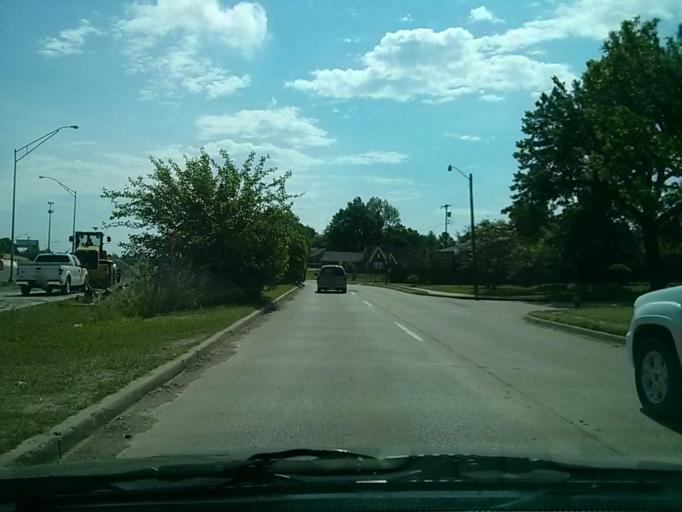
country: US
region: Oklahoma
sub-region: Tulsa County
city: Tulsa
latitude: 36.1593
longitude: -95.9452
